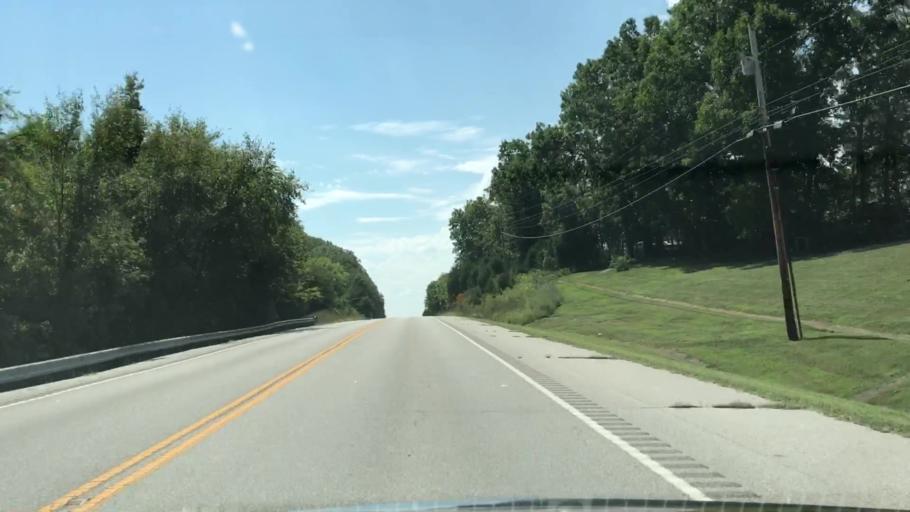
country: US
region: Tennessee
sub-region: Smith County
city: Carthage
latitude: 36.2982
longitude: -85.9998
